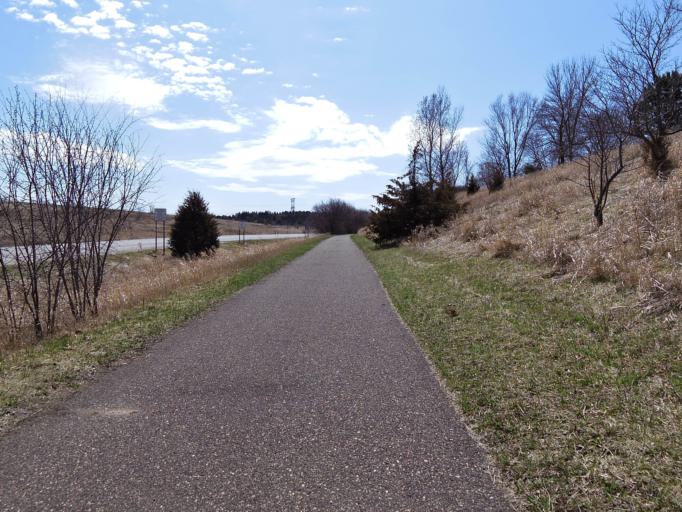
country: US
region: Minnesota
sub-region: Washington County
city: Lakeland
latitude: 44.9513
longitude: -92.8237
